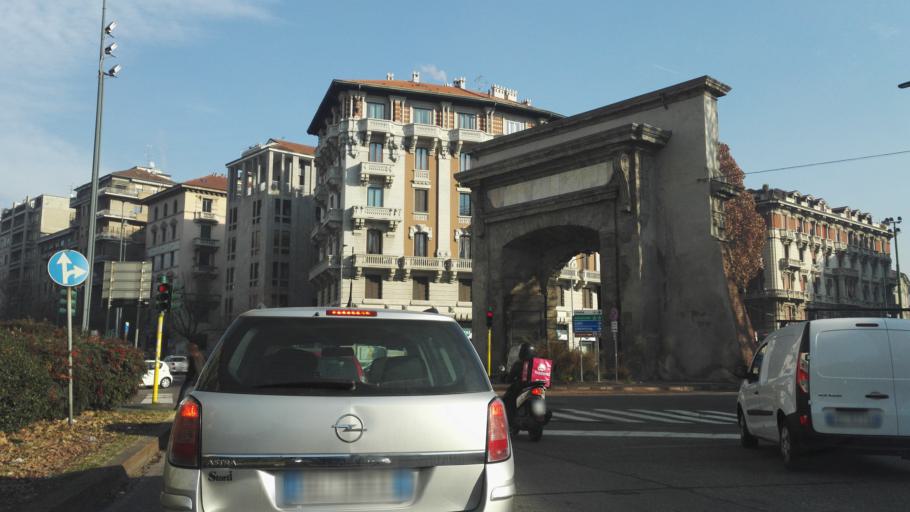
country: IT
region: Lombardy
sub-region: Citta metropolitana di Milano
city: Milano
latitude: 45.4521
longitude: 9.2015
